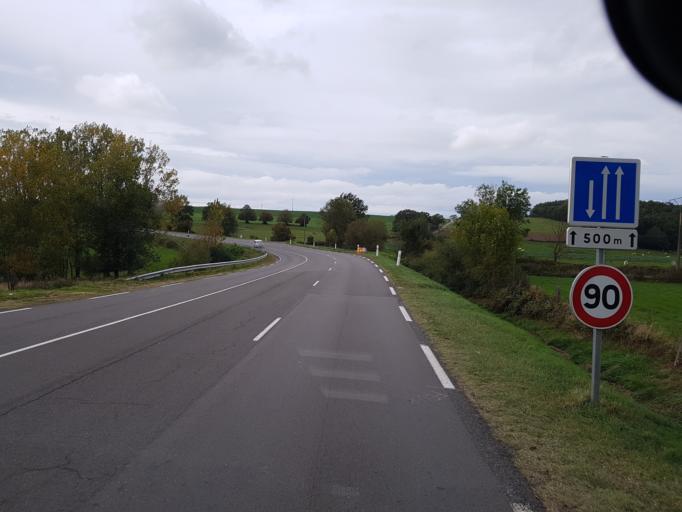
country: FR
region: Rhone-Alpes
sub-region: Departement de la Loire
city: Chazelles-sur-Lyon
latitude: 45.6357
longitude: 4.3631
